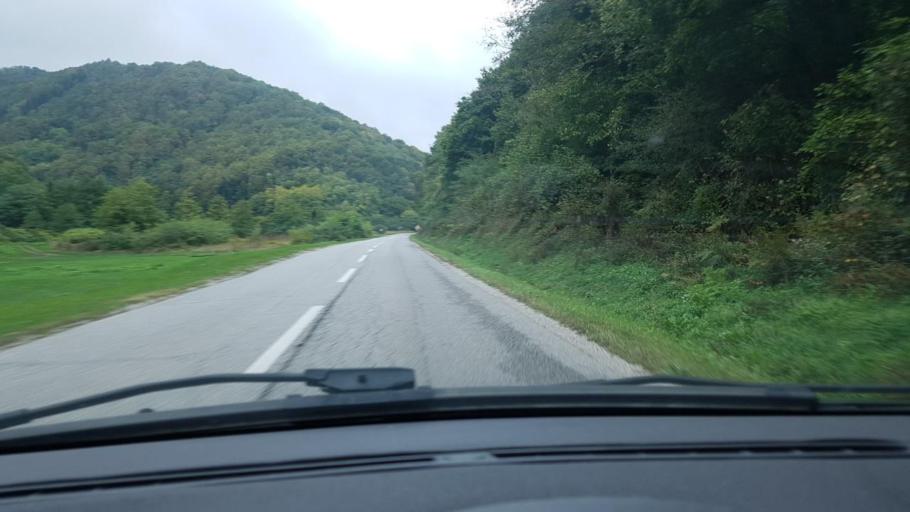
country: HR
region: Krapinsko-Zagorska
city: Marija Bistrica
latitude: 45.9324
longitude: 16.1145
